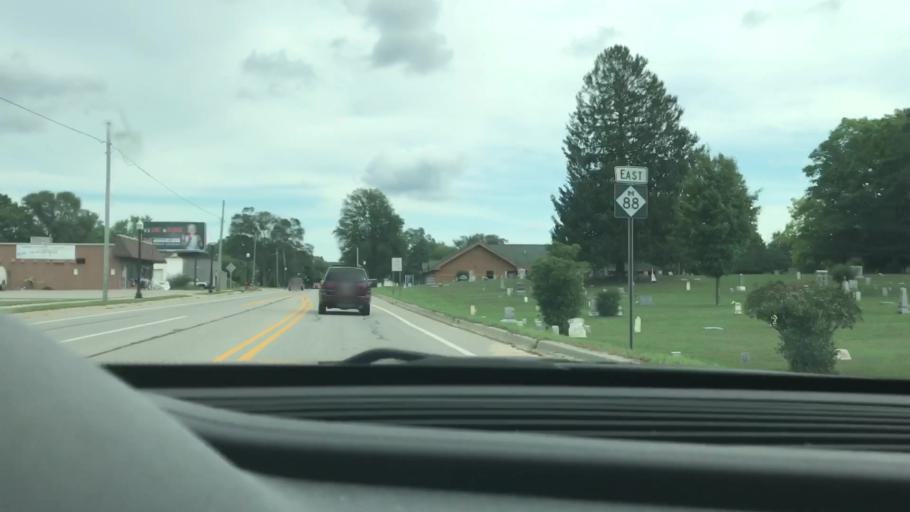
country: US
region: Michigan
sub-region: Antrim County
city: Mancelona
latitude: 44.9023
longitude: -85.0711
